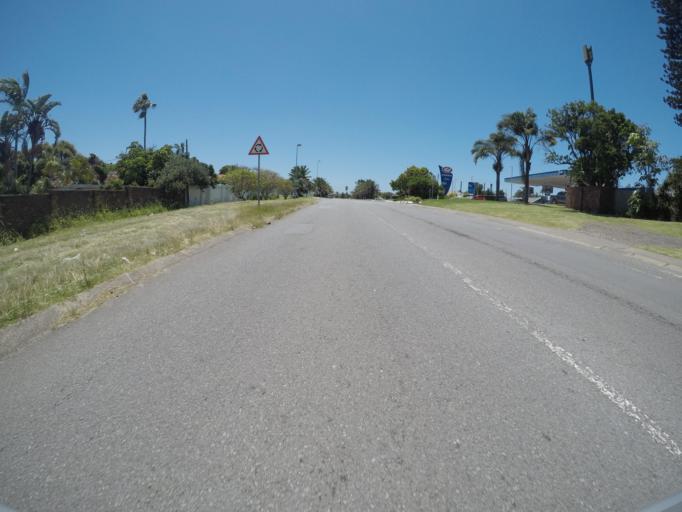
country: ZA
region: Eastern Cape
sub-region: Buffalo City Metropolitan Municipality
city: East London
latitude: -32.9768
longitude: 27.9406
